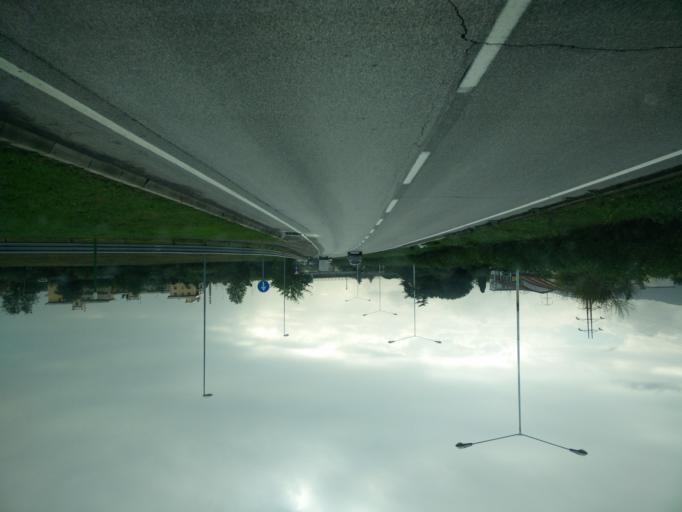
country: IT
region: Tuscany
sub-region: Provincia di Prato
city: Prato
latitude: 43.8761
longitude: 11.0757
